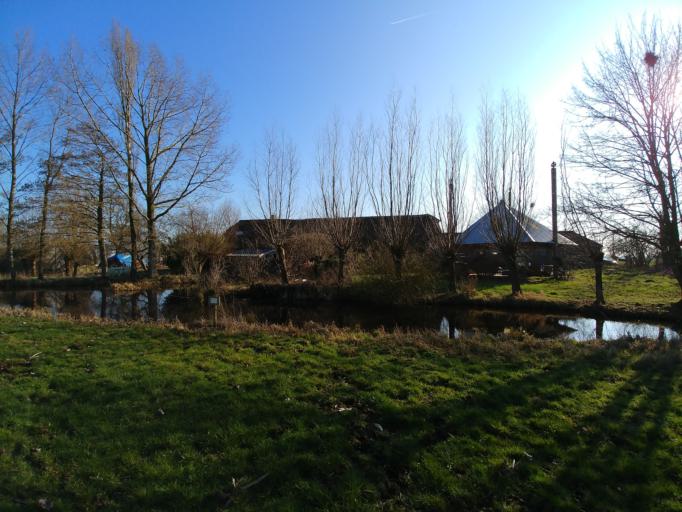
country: NL
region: Utrecht
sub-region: Gemeente Woerden
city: Woerden
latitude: 52.1479
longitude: 4.9024
